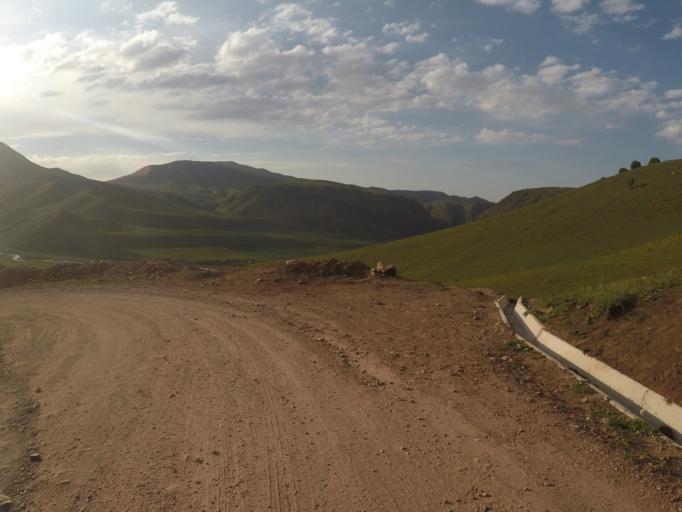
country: KG
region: Chuy
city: Bishkek
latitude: 42.6308
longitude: 74.6205
